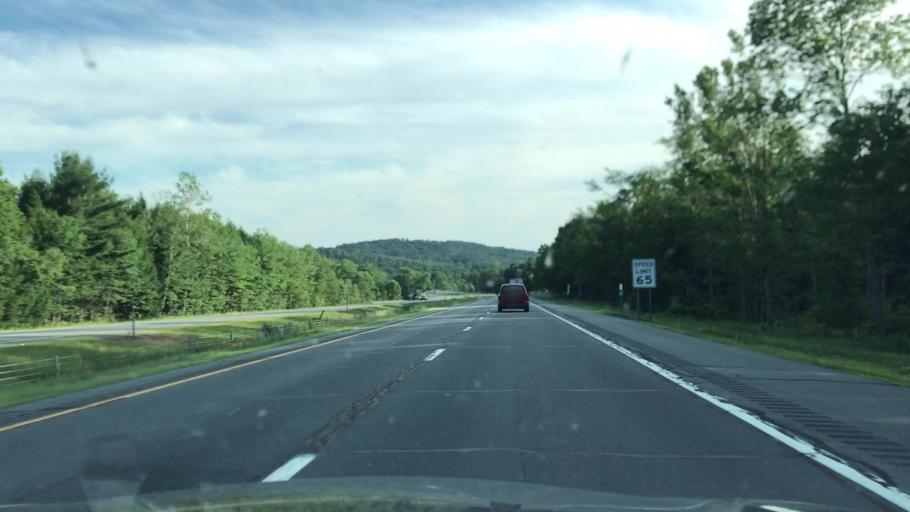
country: US
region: New York
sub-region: Sullivan County
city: Monticello
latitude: 41.7125
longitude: -74.7329
